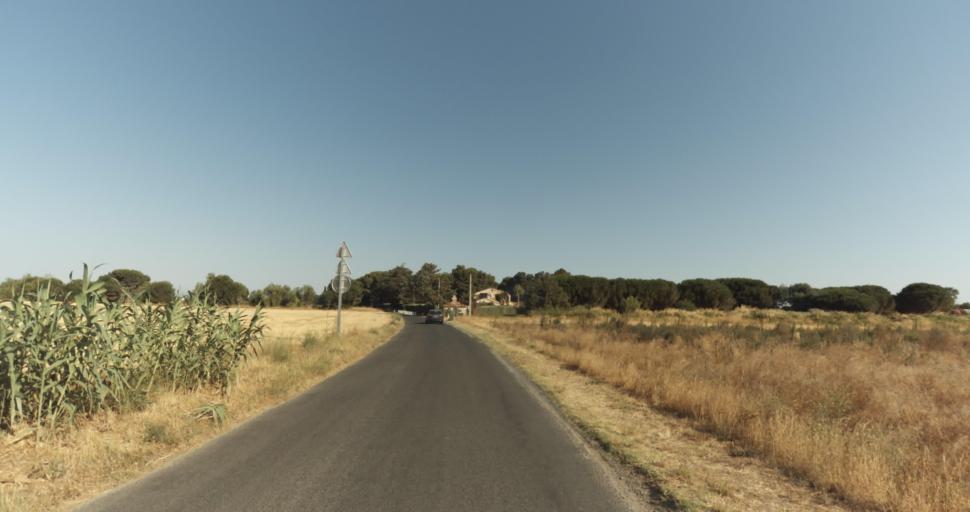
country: FR
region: Languedoc-Roussillon
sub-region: Departement des Pyrenees-Orientales
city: Alenya
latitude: 42.6444
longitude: 2.9747
